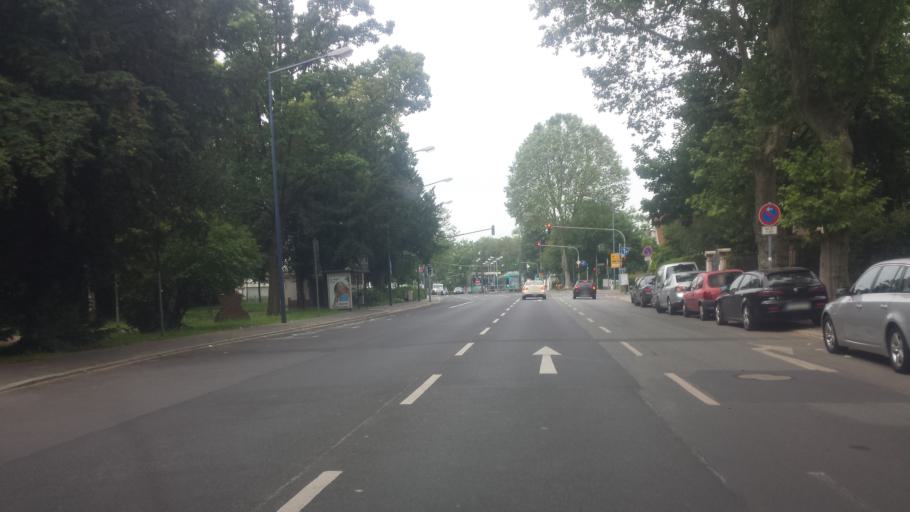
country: DE
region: Hesse
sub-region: Regierungsbezirk Darmstadt
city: Offenbach
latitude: 50.1023
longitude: 8.7467
